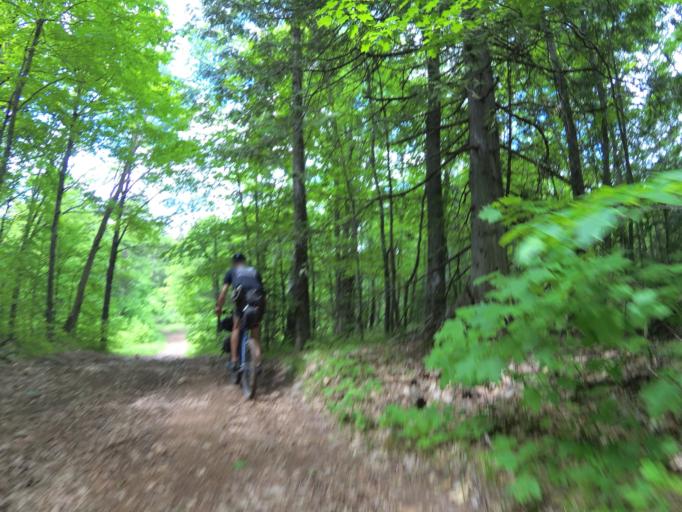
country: CA
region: Ontario
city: Renfrew
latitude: 45.0731
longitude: -76.7958
